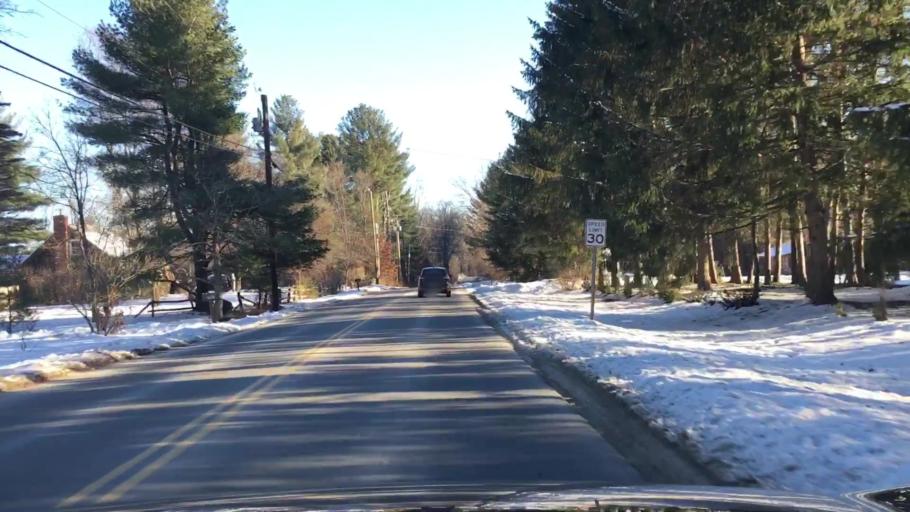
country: US
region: New Hampshire
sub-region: Hillsborough County
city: Milford
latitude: 42.8291
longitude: -71.5877
